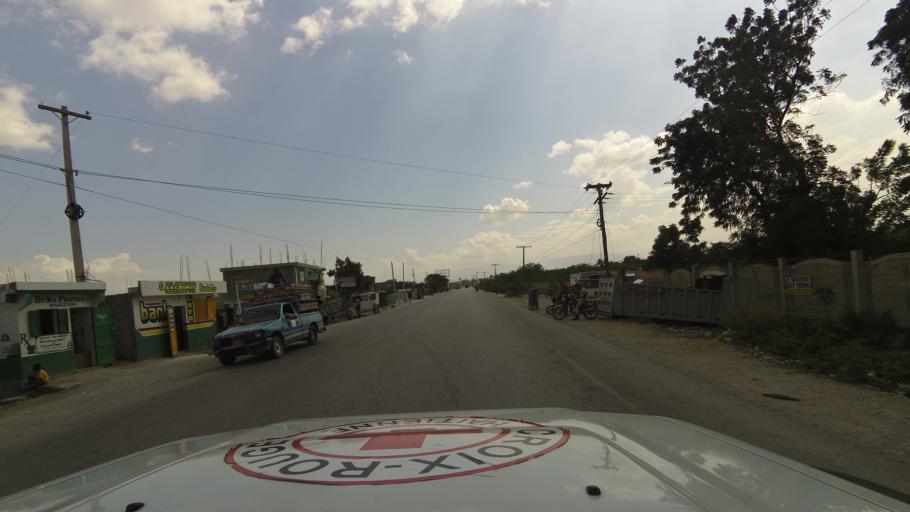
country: HT
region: Ouest
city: Croix des Bouquets
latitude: 18.6441
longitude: -72.2753
